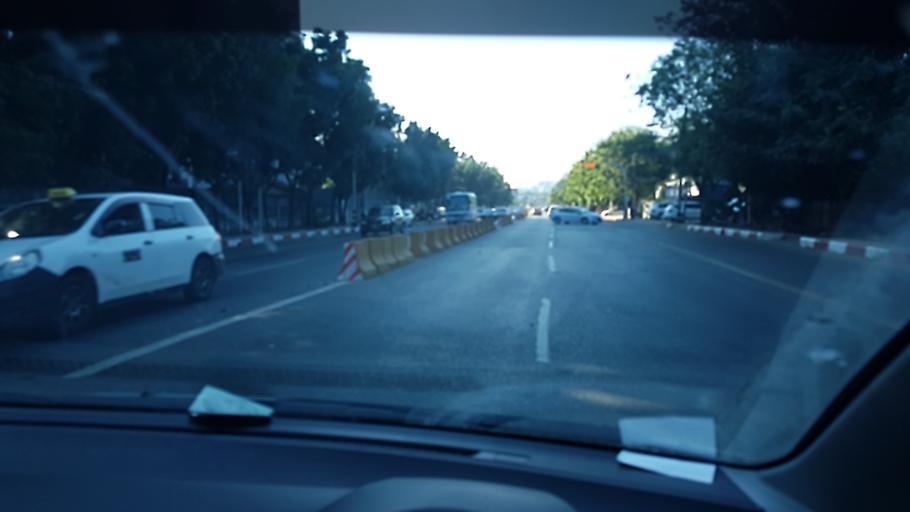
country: MM
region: Yangon
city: Yangon
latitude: 16.8455
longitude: 96.1359
